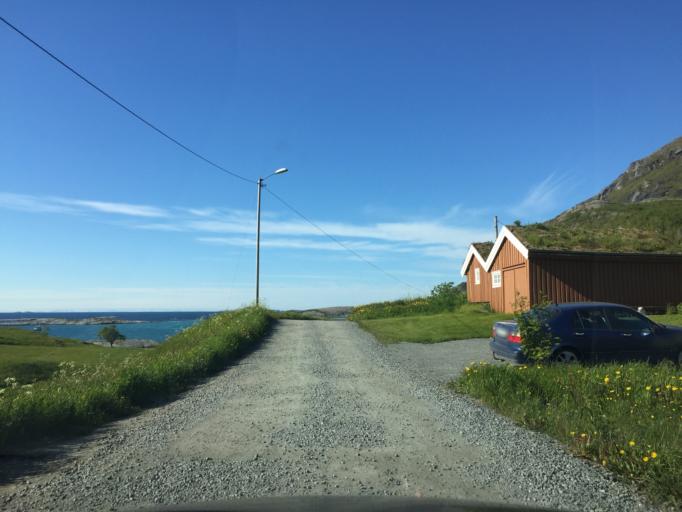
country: NO
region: Nordland
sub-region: Bodo
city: Loding
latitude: 67.4096
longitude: 14.6280
